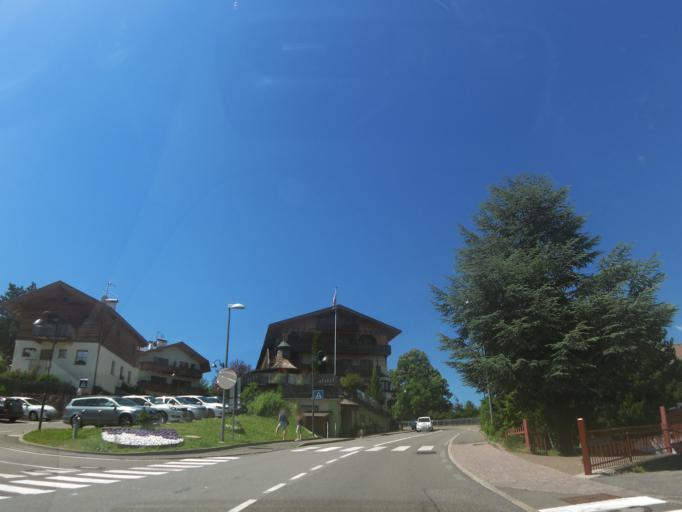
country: IT
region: Trentino-Alto Adige
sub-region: Bolzano
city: Castelrotto
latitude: 46.5647
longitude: 11.5583
